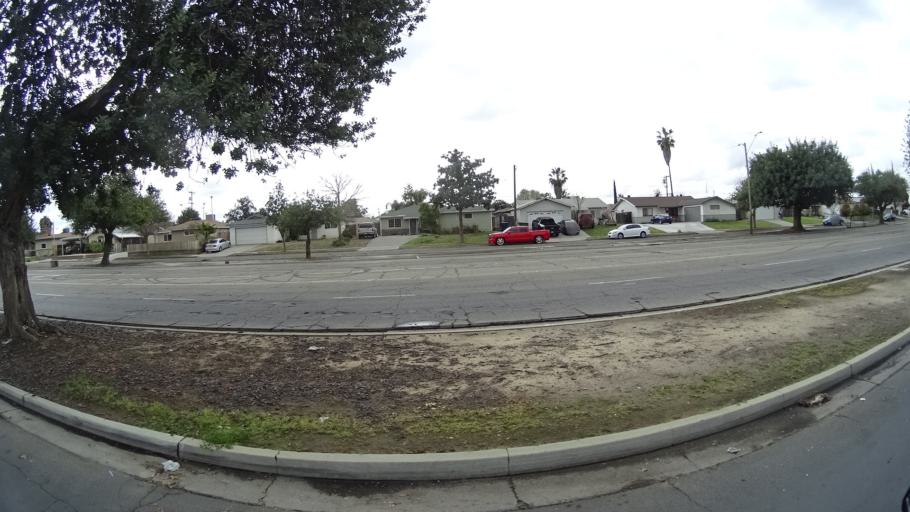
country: US
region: California
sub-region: Fresno County
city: West Park
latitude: 36.7795
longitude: -119.8379
